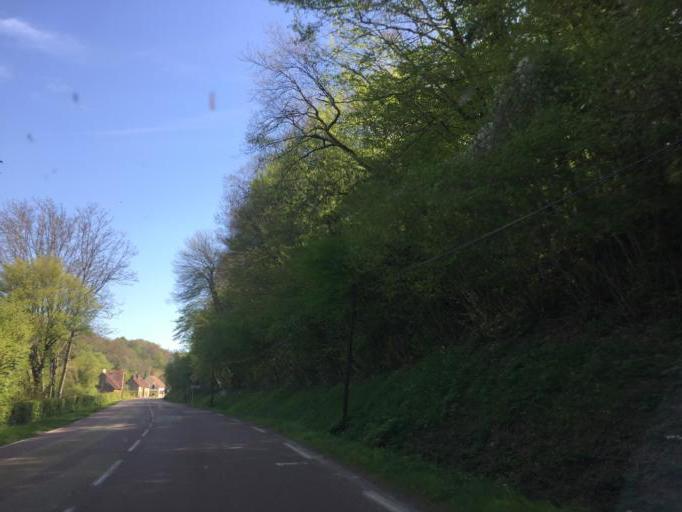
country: FR
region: Bourgogne
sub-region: Departement de la Nievre
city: Clamecy
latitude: 47.4550
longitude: 3.6592
